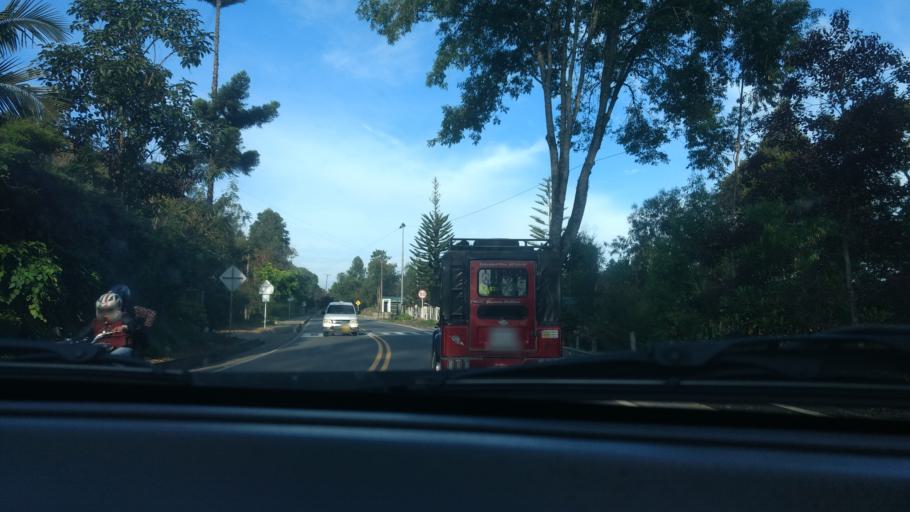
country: CO
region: Cauca
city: Rosas
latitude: 2.3071
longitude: -76.6976
